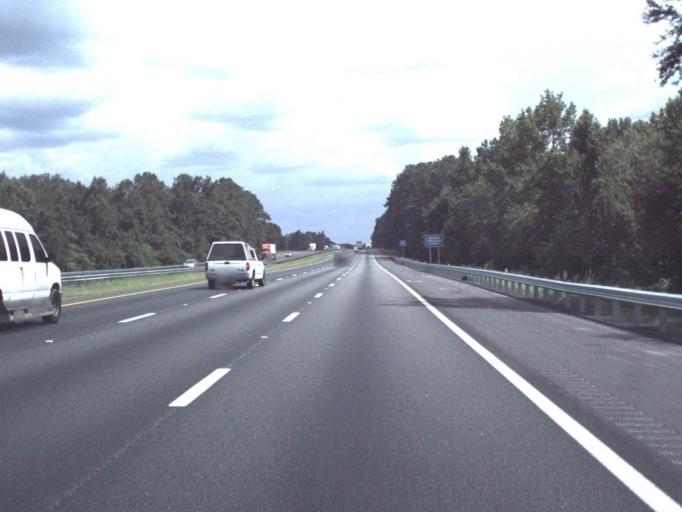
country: US
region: Florida
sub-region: Alachua County
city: High Springs
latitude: 29.9259
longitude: -82.5586
